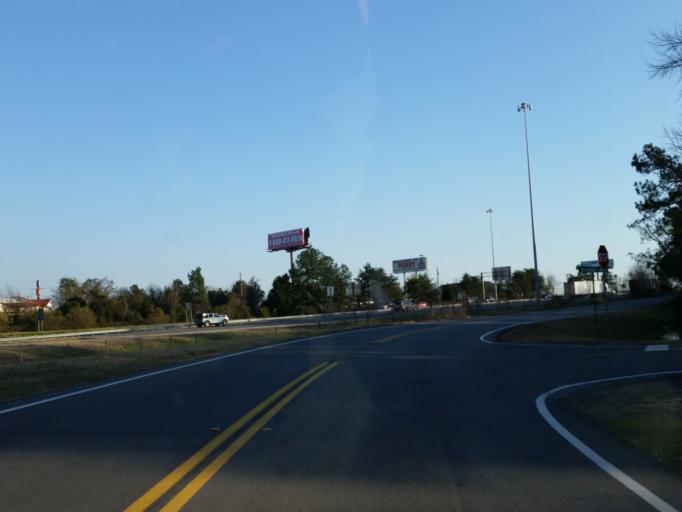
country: US
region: Georgia
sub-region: Houston County
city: Perry
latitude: 32.4458
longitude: -83.7557
